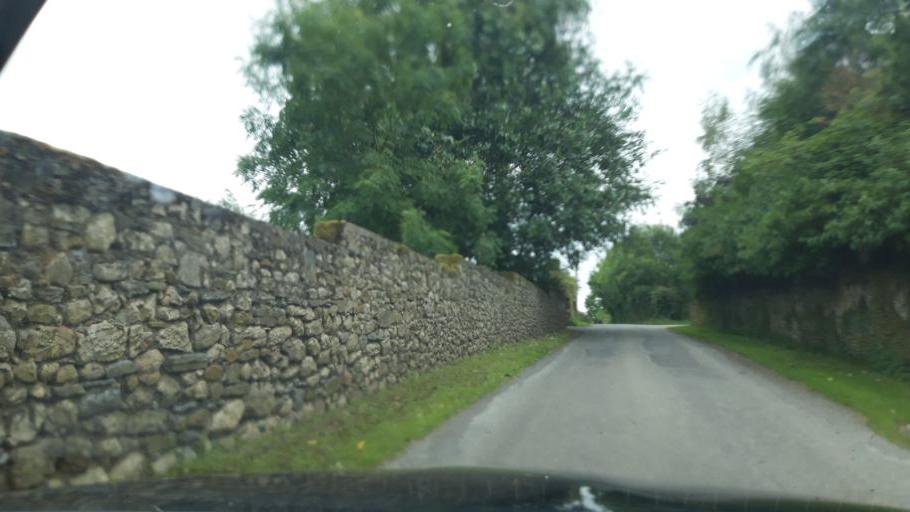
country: IE
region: Leinster
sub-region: Kilkenny
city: Thomastown
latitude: 52.6262
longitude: -7.0670
